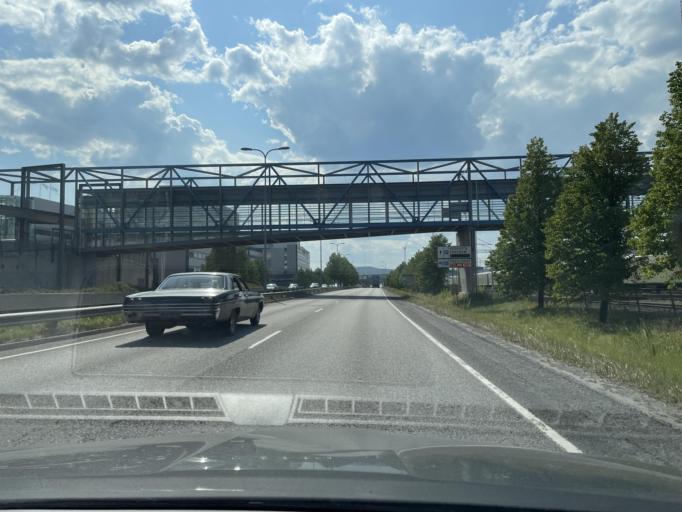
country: FI
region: Central Finland
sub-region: Jyvaeskylae
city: Jyvaeskylae
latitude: 62.2413
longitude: 25.7566
